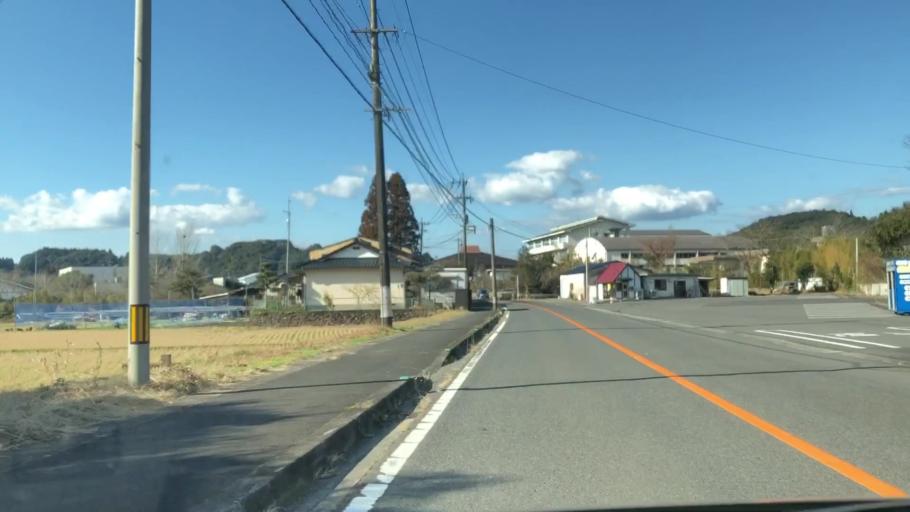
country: JP
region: Kagoshima
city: Satsumasendai
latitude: 31.8002
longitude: 130.4378
